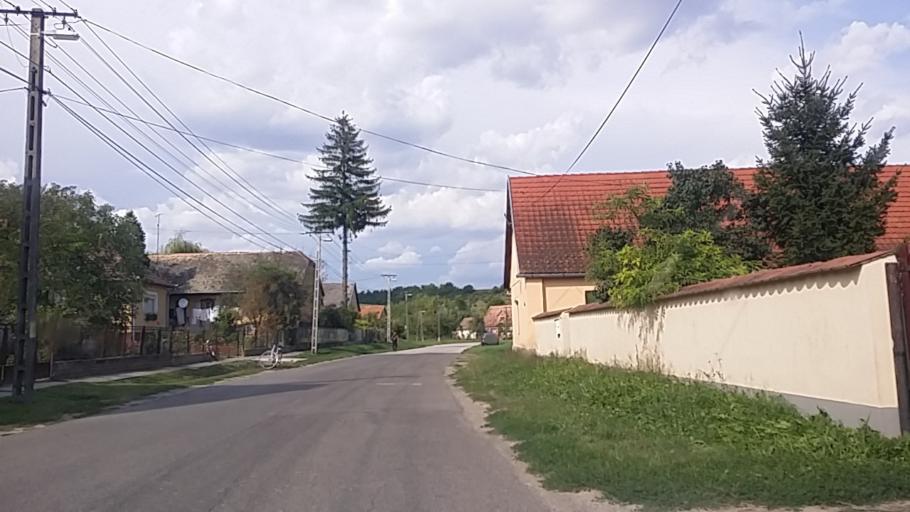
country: HU
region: Tolna
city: Zomba
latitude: 46.5023
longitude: 18.5680
